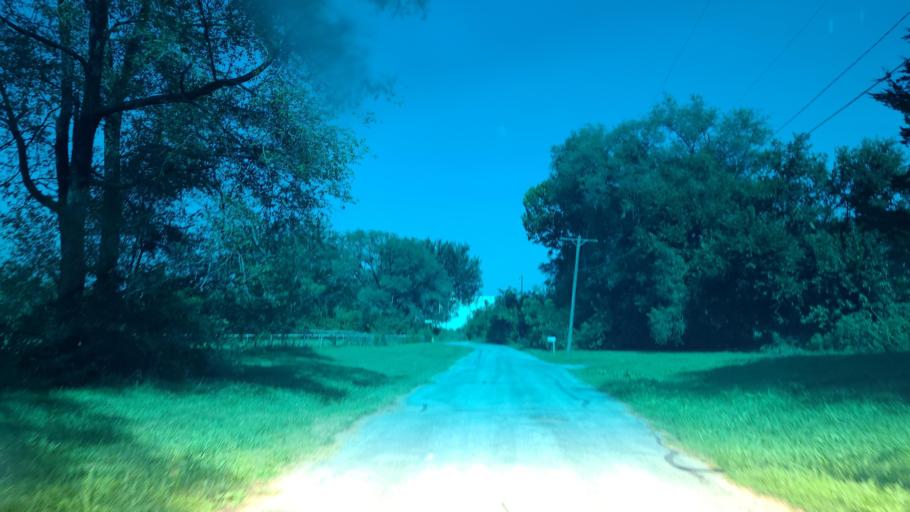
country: US
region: Kansas
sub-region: Douglas County
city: Lawrence
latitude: 38.9806
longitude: -95.2179
